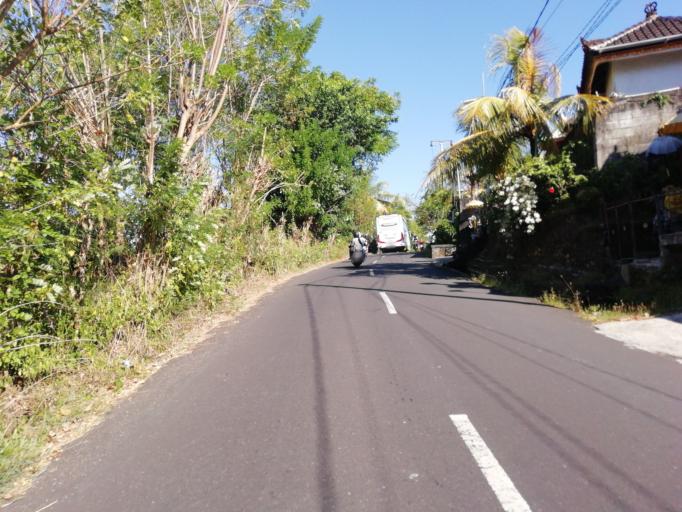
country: ID
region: Bali
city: Jimbaran
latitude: -8.8324
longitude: 115.1776
